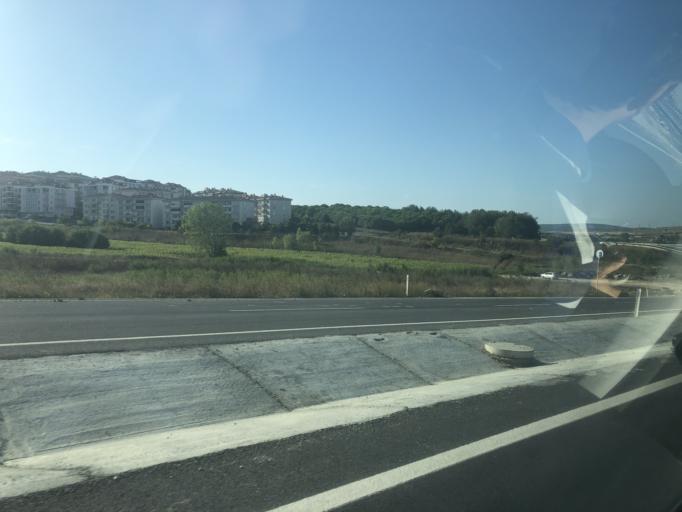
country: TR
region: Istanbul
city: Catalca
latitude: 41.1397
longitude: 28.4764
